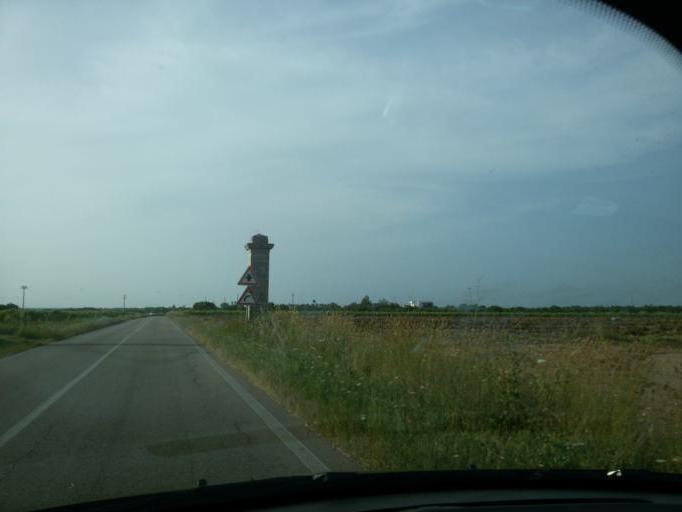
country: IT
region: Apulia
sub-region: Provincia di Brindisi
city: San Pancrazio Salentino
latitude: 40.3931
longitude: 17.8349
